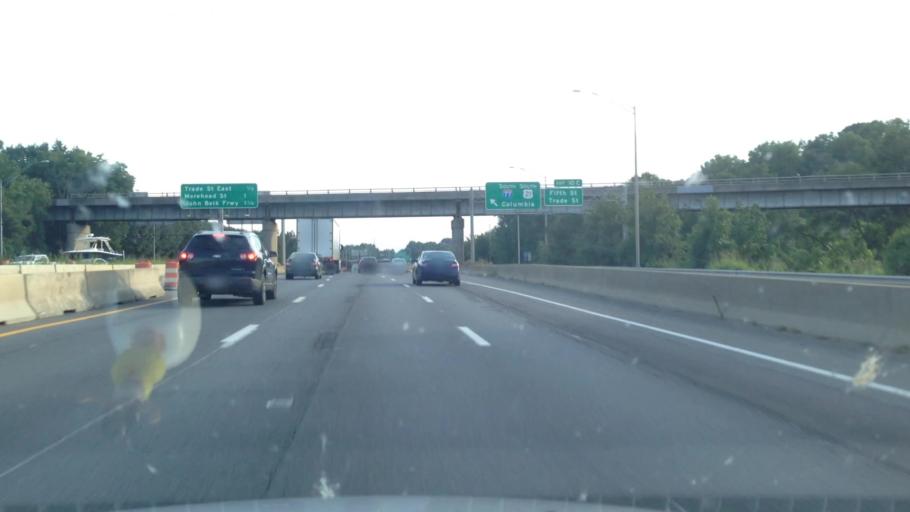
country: US
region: North Carolina
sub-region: Mecklenburg County
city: Charlotte
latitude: 35.2420
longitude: -80.8499
